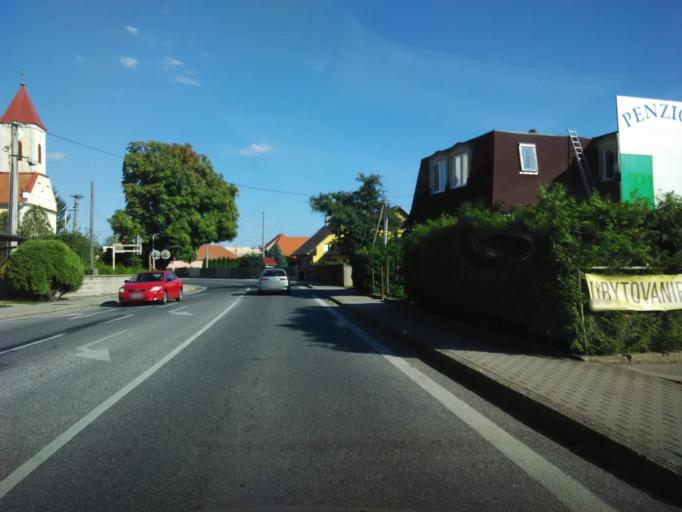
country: SK
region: Nitriansky
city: Tlmace
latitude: 48.2894
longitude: 18.5315
